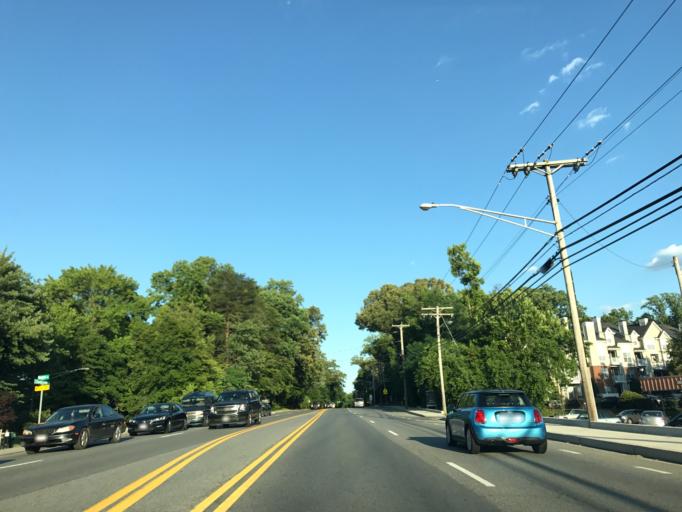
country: US
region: Maryland
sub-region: Anne Arundel County
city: Crofton
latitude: 39.0179
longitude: -76.6931
